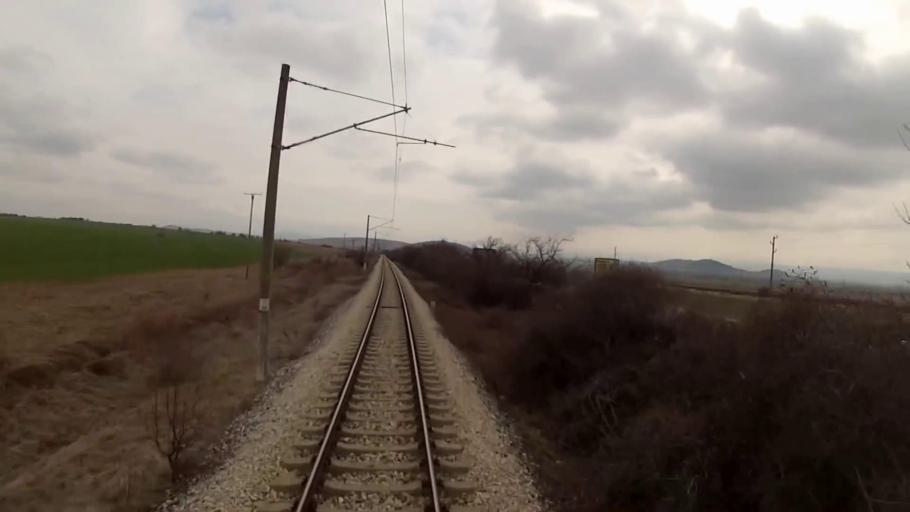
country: BG
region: Sofiya
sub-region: Obshtina Gorna Malina
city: Gorna Malina
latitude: 42.6984
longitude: 23.6714
